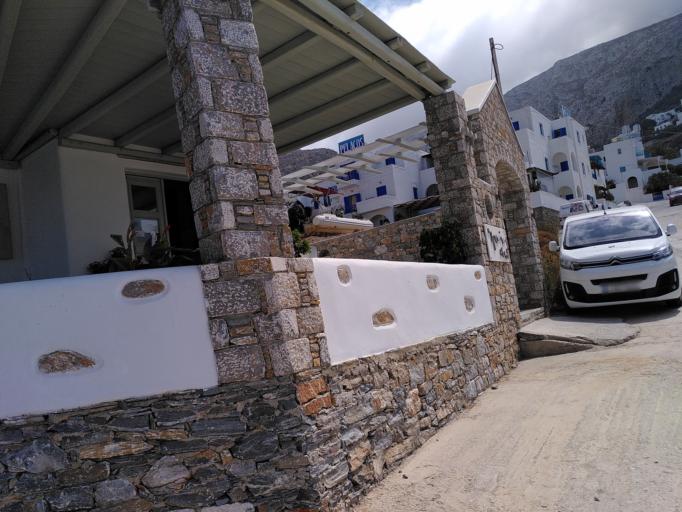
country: GR
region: South Aegean
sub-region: Nomos Kykladon
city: Amorgos
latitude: 36.8999
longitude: 25.9757
